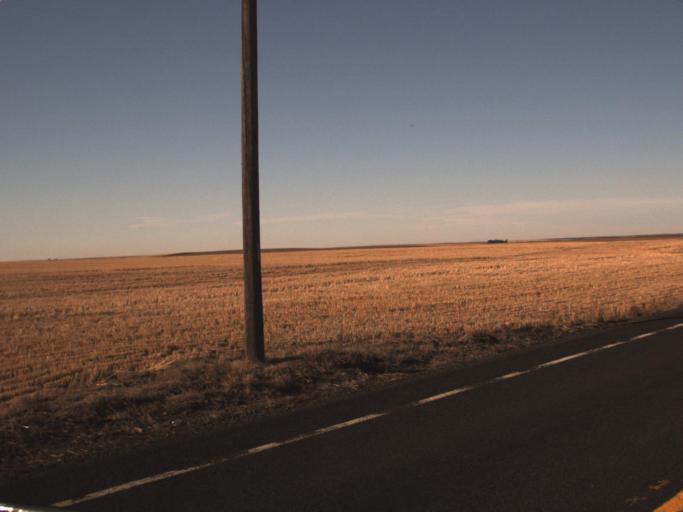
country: US
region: Washington
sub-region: Adams County
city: Ritzville
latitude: 46.8886
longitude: -118.3342
